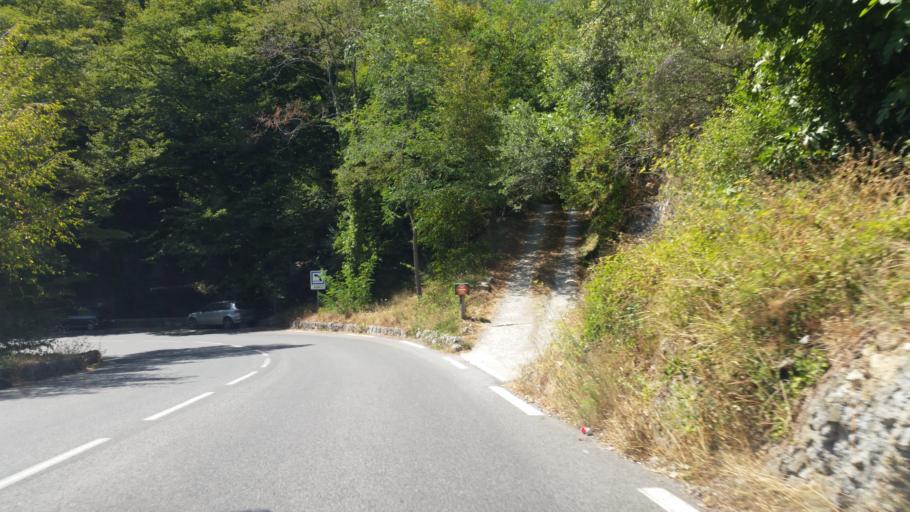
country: FR
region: Provence-Alpes-Cote d'Azur
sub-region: Departement des Alpes-Maritimes
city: Sainte-Agnes
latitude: 43.8267
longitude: 7.4779
